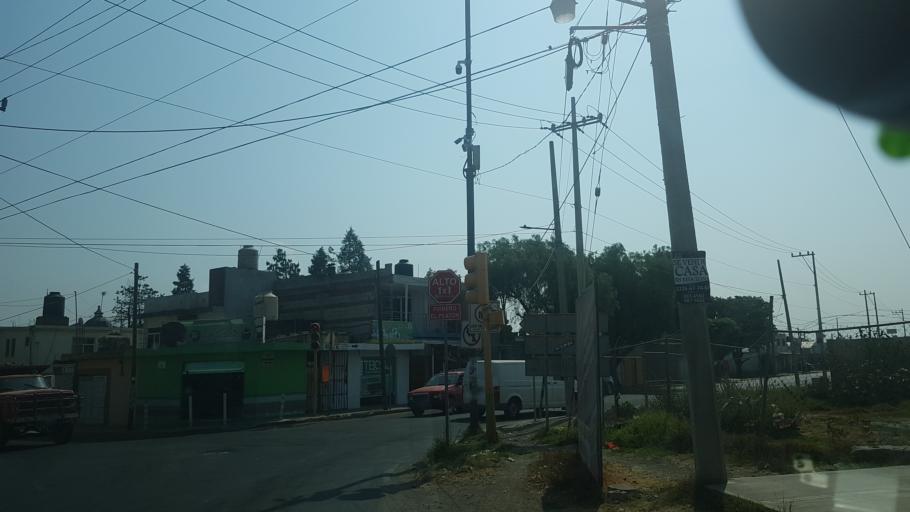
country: MX
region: Puebla
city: Cholula
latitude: 19.0584
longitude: -98.3186
